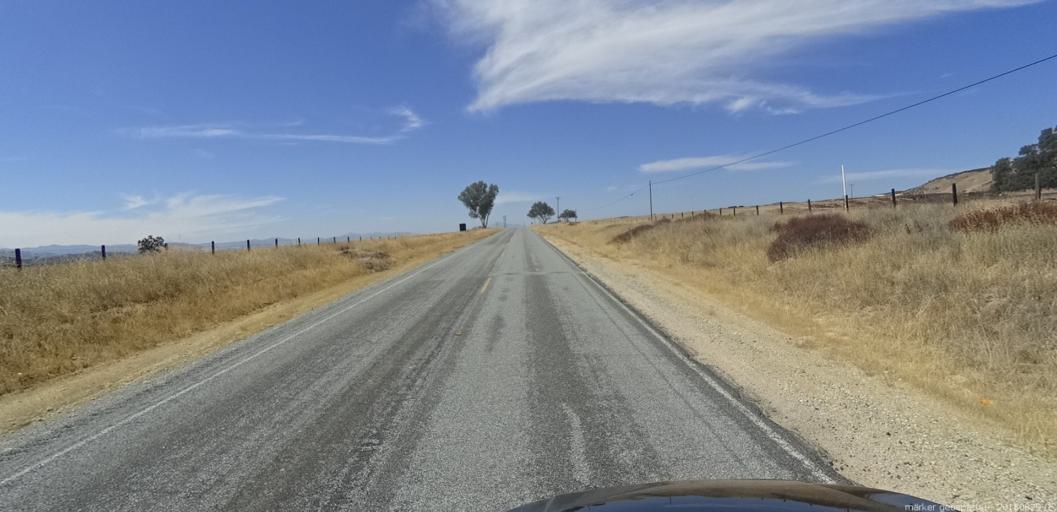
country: US
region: California
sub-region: San Luis Obispo County
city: Lake Nacimiento
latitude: 35.9201
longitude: -121.0339
